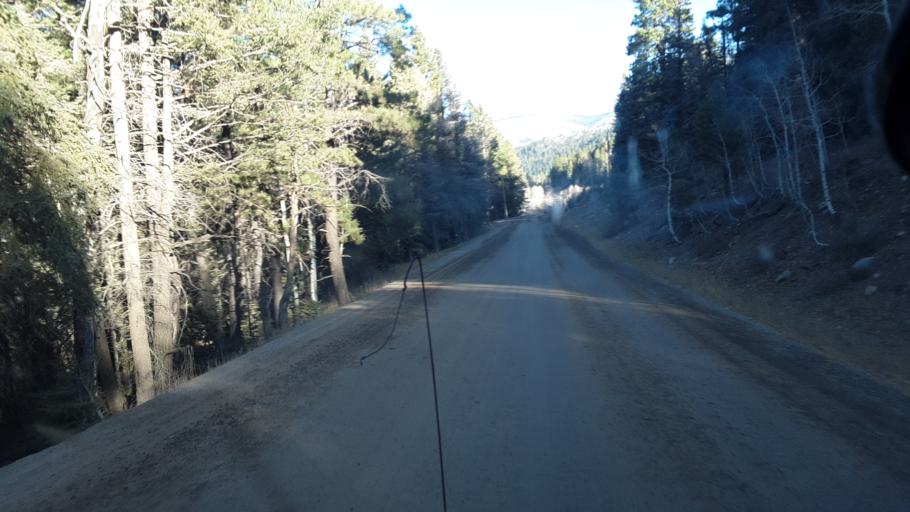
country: US
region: Colorado
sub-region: La Plata County
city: Bayfield
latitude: 37.4069
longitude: -107.6612
